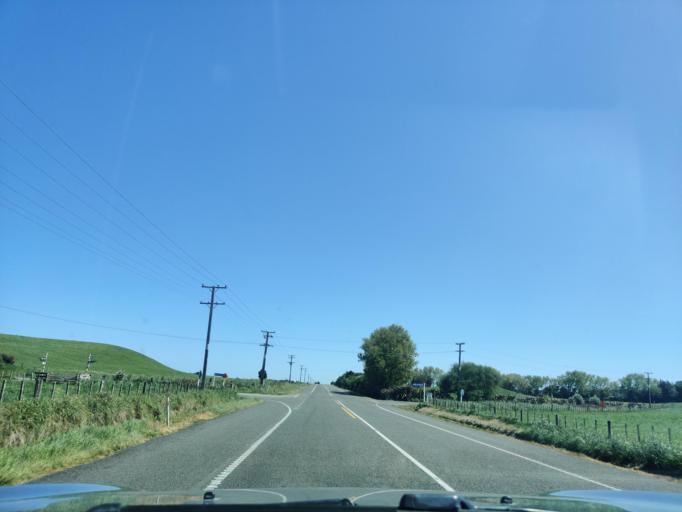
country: NZ
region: Taranaki
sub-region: South Taranaki District
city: Patea
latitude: -39.7739
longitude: 174.6766
